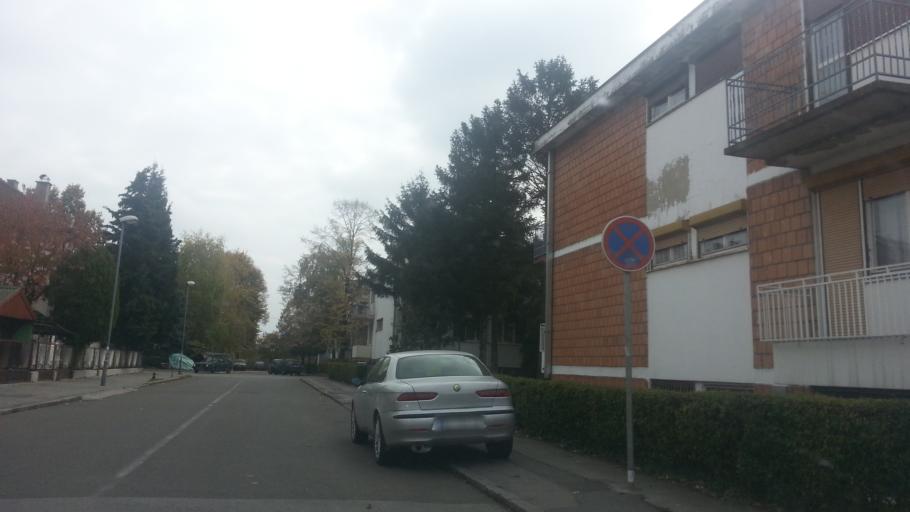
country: RS
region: Central Serbia
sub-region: Belgrade
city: Zemun
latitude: 44.8578
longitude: 20.3707
